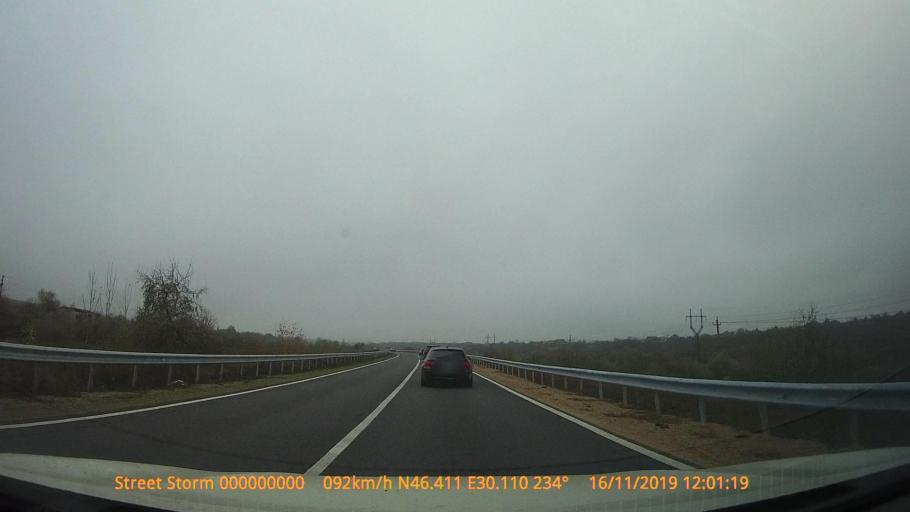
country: UA
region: Odessa
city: Bilyayivka
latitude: 46.4103
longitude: 30.1098
